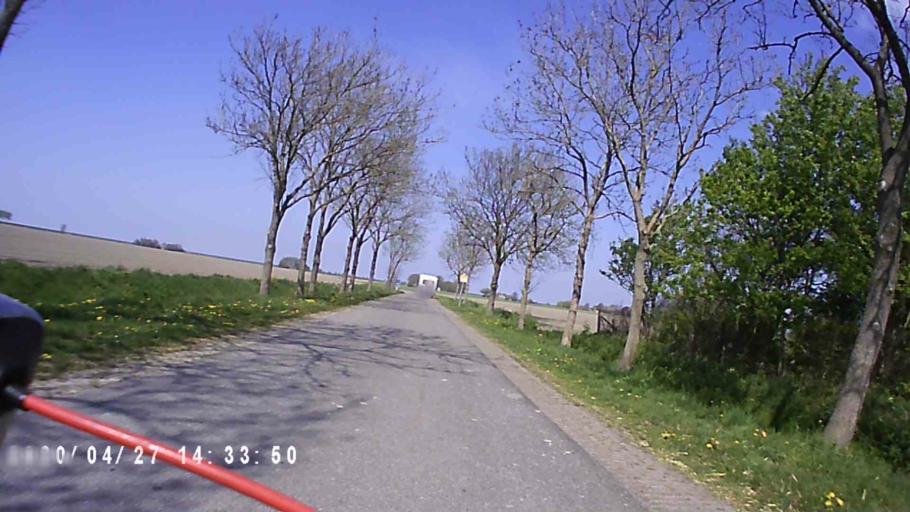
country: NL
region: Groningen
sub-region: Gemeente Zuidhorn
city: Oldehove
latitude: 53.3945
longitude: 6.4246
